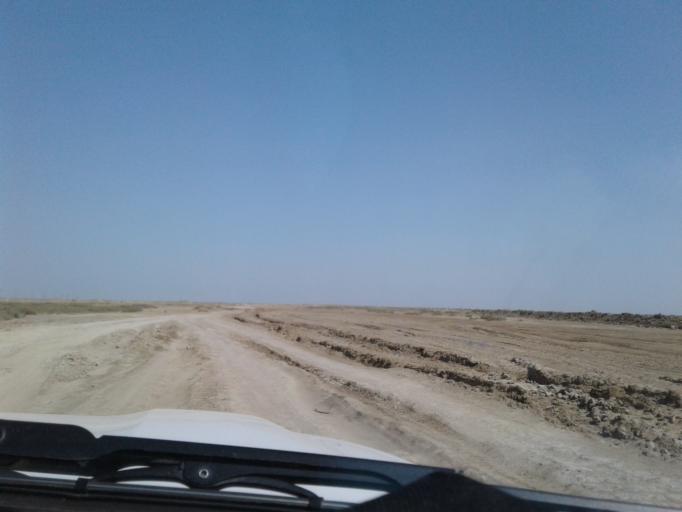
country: IR
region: Golestan
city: Gomishan
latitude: 37.8212
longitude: 53.9223
